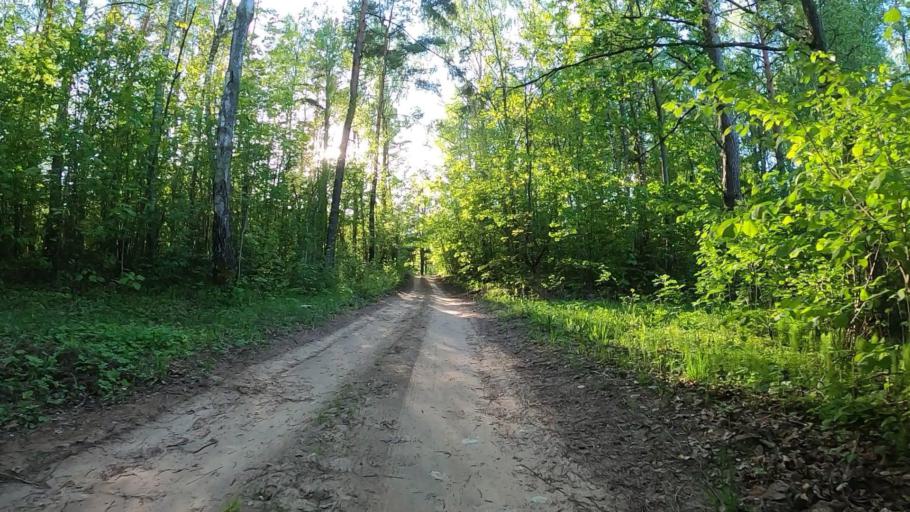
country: LV
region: Kekava
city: Kekava
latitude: 56.7768
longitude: 24.2921
